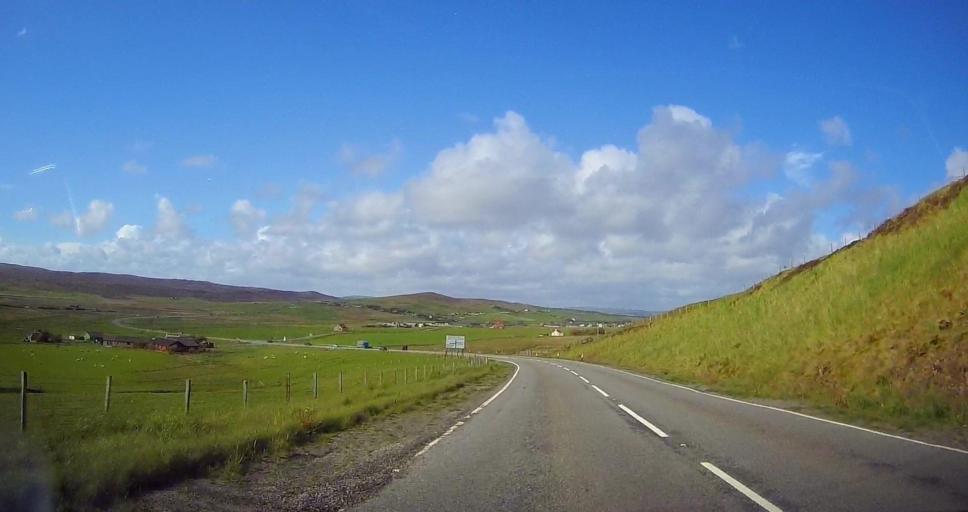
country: GB
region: Scotland
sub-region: Shetland Islands
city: Lerwick
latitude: 60.1822
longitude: -1.2246
